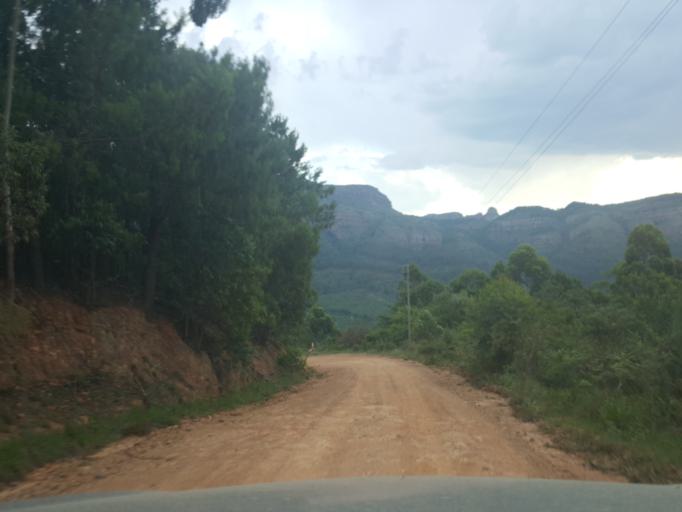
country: ZA
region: Limpopo
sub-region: Mopani District Municipality
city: Hoedspruit
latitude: -24.5888
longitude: 30.8674
